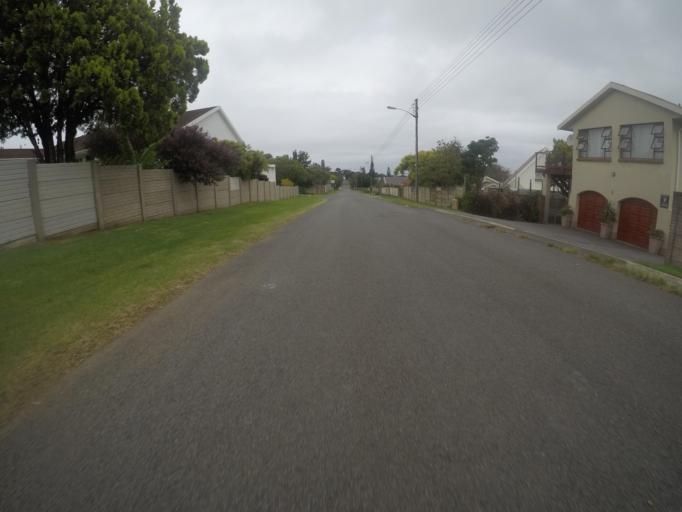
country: ZA
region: Eastern Cape
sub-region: Buffalo City Metropolitan Municipality
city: East London
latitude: -32.9391
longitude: 28.0035
